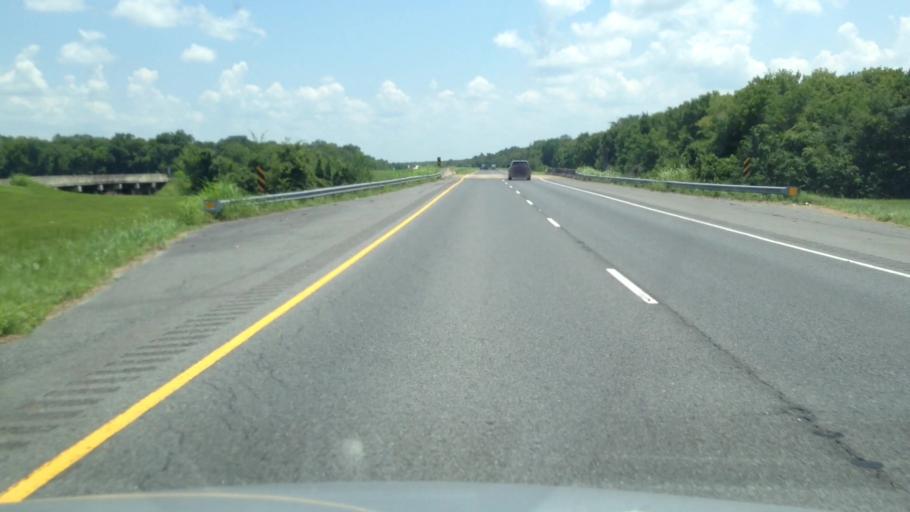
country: US
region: Louisiana
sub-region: Avoyelles Parish
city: Bunkie
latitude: 30.8222
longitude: -92.2233
